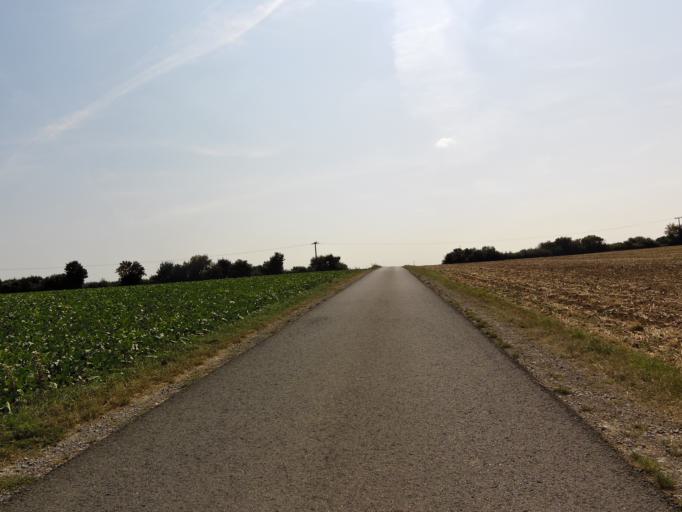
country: DE
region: Bavaria
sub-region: Regierungsbezirk Unterfranken
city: Rottendorf
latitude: 49.7754
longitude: 10.0294
